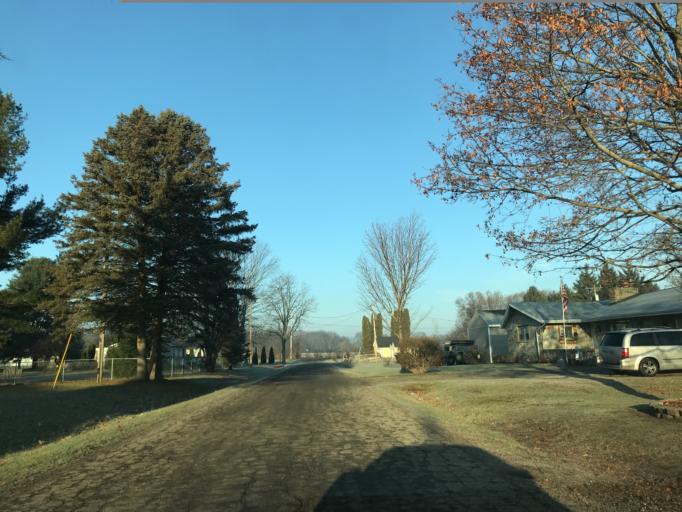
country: US
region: Michigan
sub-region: Eaton County
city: Eaton Rapids
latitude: 42.4452
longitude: -84.5654
